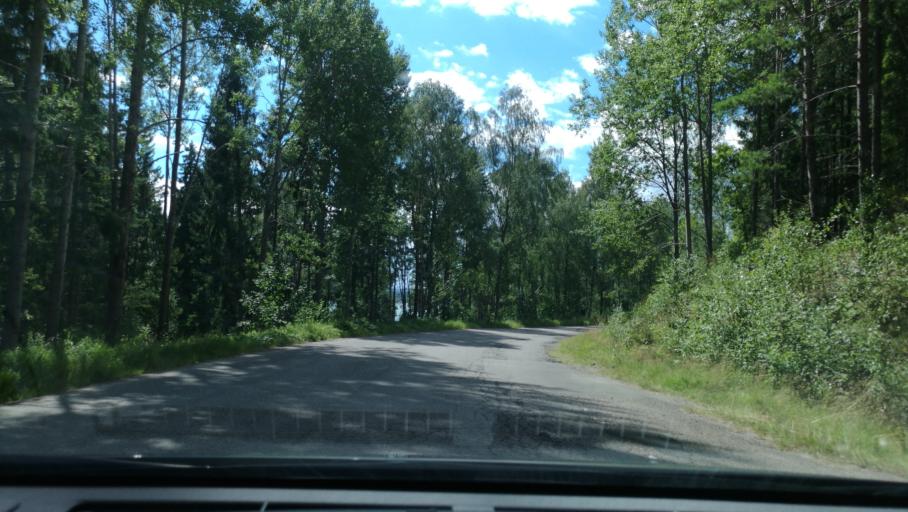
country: SE
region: OEstergoetland
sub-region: Norrkopings Kommun
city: Krokek
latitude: 58.6624
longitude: 16.4682
